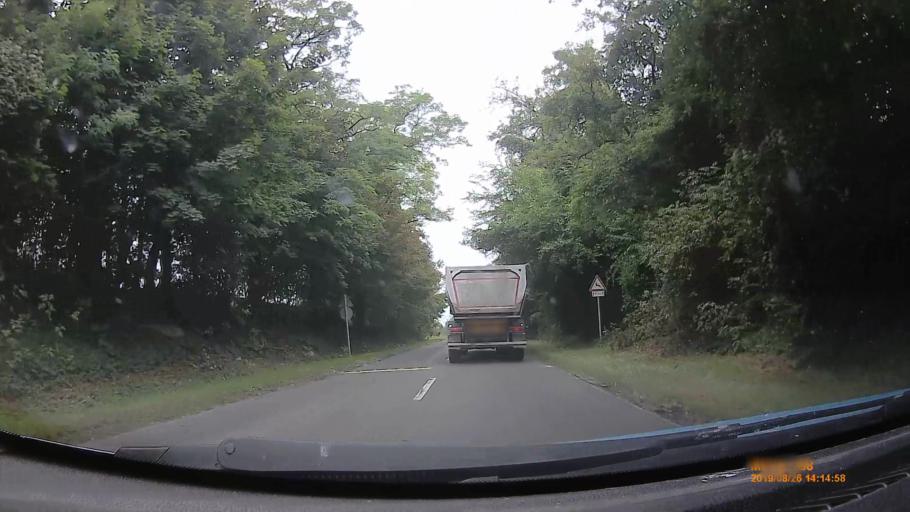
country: HU
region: Fejer
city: Csakvar
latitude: 47.4272
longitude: 18.5218
